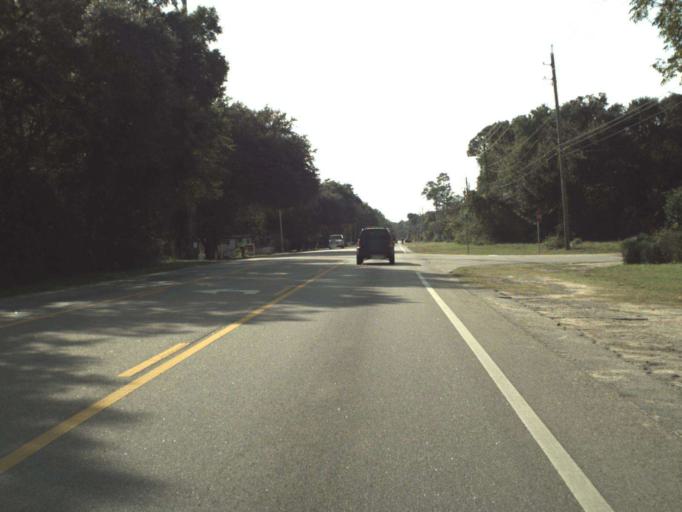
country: US
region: Florida
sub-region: Escambia County
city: Warrington
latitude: 30.3822
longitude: -87.3043
